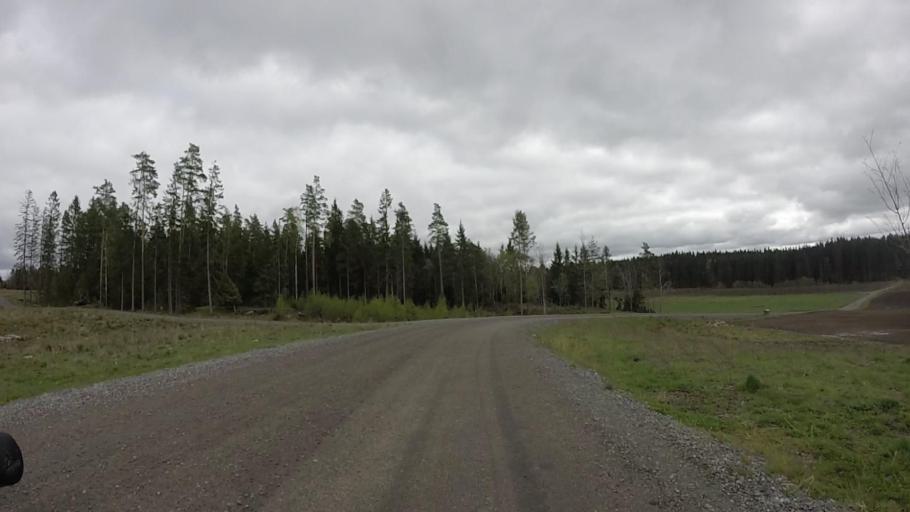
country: SE
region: Vaestra Goetaland
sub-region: Trollhattan
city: Sjuntorp
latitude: 58.2243
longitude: 12.2161
